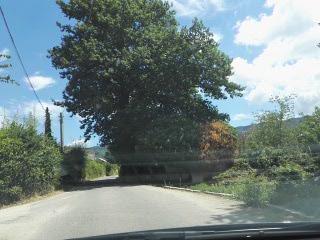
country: IT
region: Calabria
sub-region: Provincia di Vibo-Valentia
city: Serra San Bruno
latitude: 38.5757
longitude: 16.3188
